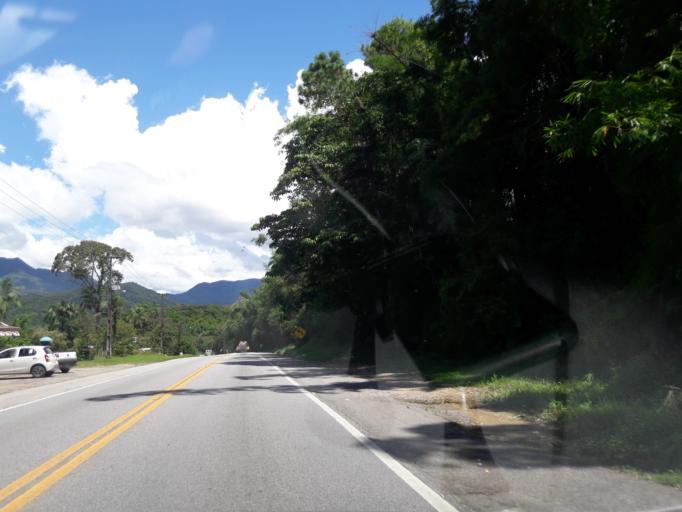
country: BR
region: Parana
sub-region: Antonina
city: Antonina
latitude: -25.5374
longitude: -48.7940
